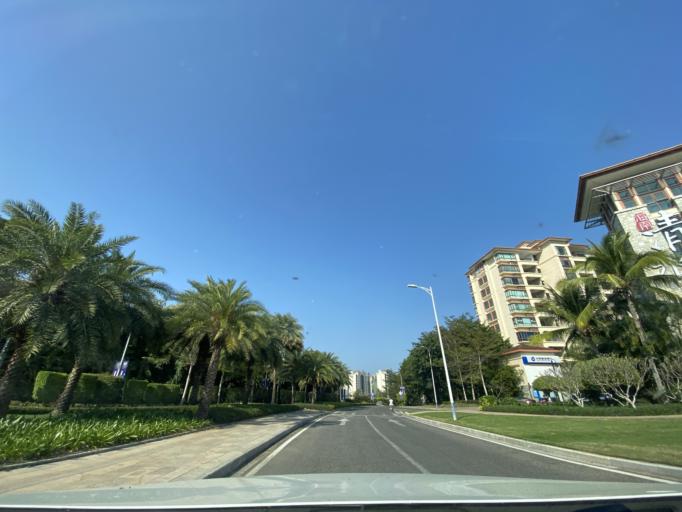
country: CN
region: Hainan
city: Yingzhou
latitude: 18.4079
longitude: 109.8484
